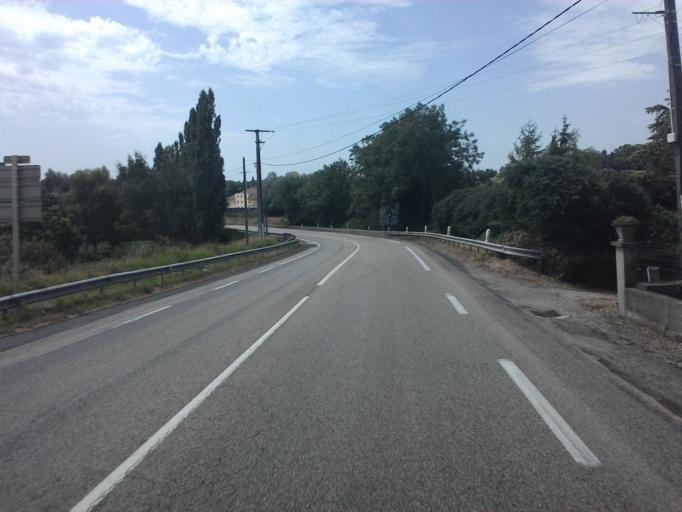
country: FR
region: Rhone-Alpes
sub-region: Departement de l'Ain
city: Saint-Etienne-du-Bois
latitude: 46.3322
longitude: 5.3148
